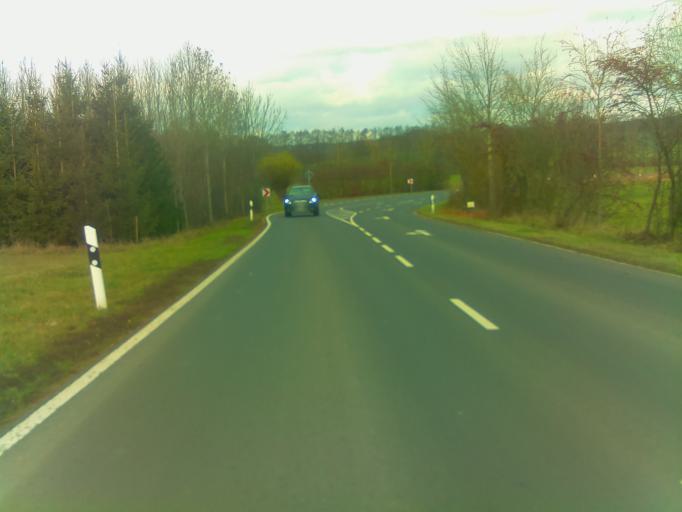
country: DE
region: Thuringia
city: Gleichamberg
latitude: 50.3735
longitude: 10.6450
